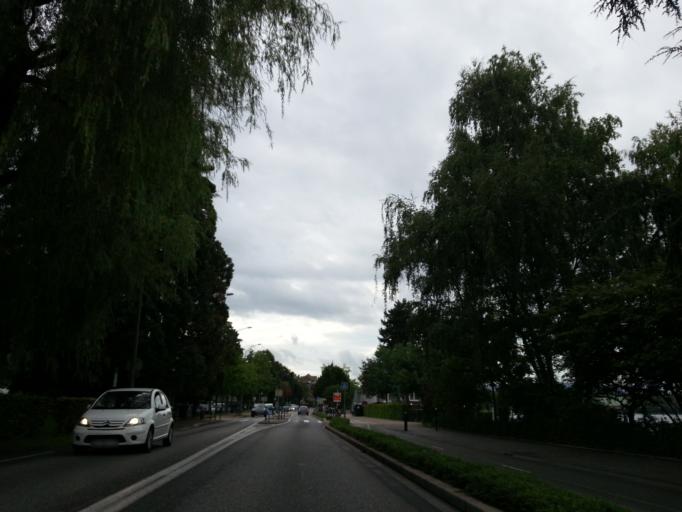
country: FR
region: Rhone-Alpes
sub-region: Departement de la Haute-Savoie
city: Annecy
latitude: 45.8923
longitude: 6.1377
